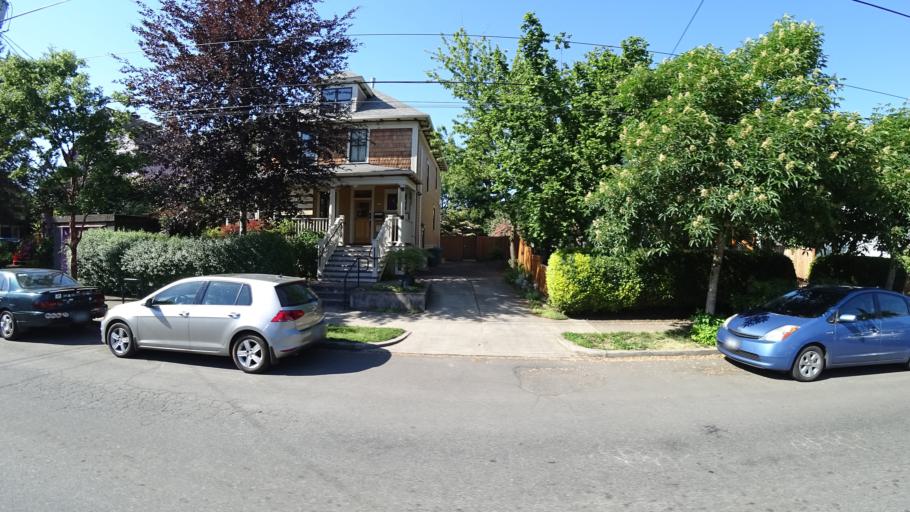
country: US
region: Oregon
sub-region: Multnomah County
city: Portland
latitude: 45.5421
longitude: -122.6606
